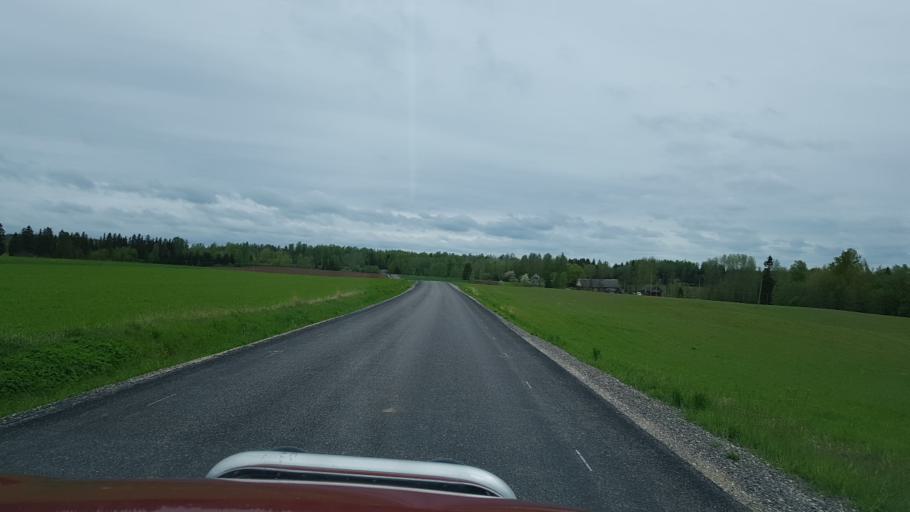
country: EE
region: Tartu
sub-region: Puhja vald
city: Puhja
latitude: 58.3058
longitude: 26.3898
